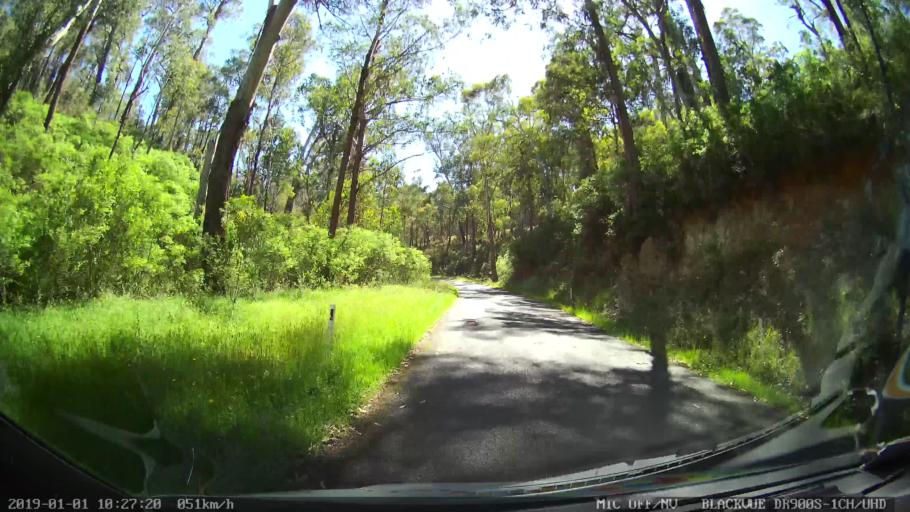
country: AU
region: New South Wales
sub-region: Snowy River
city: Jindabyne
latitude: -36.0666
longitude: 148.2361
